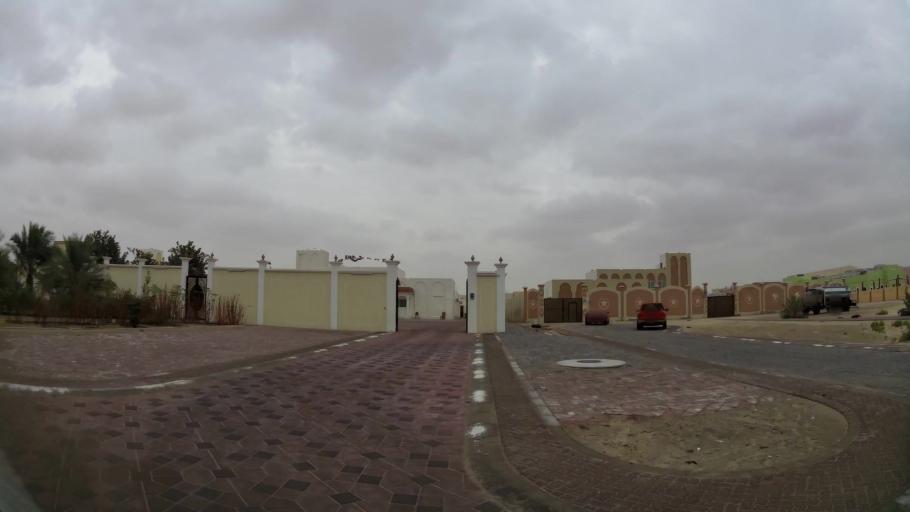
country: AE
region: Abu Dhabi
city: Abu Dhabi
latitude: 24.3308
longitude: 54.6427
